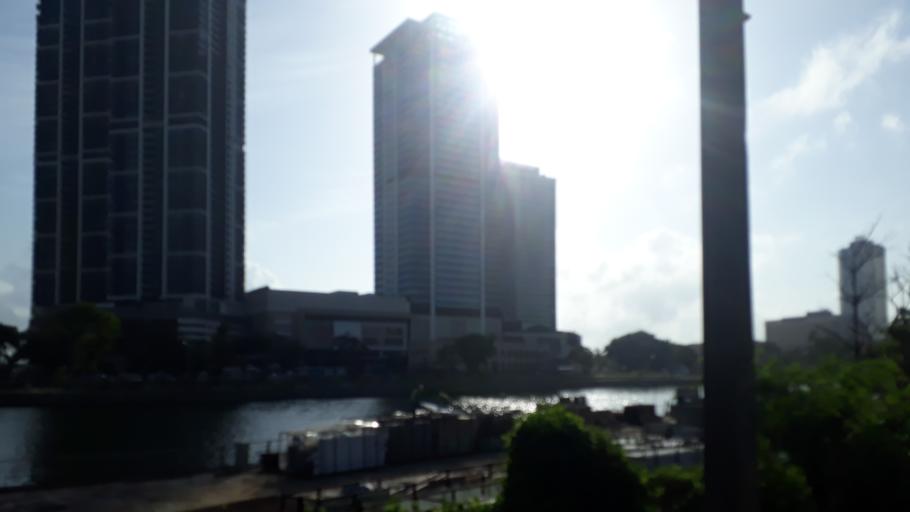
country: LK
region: Western
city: Colombo
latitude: 6.9268
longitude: 79.8483
